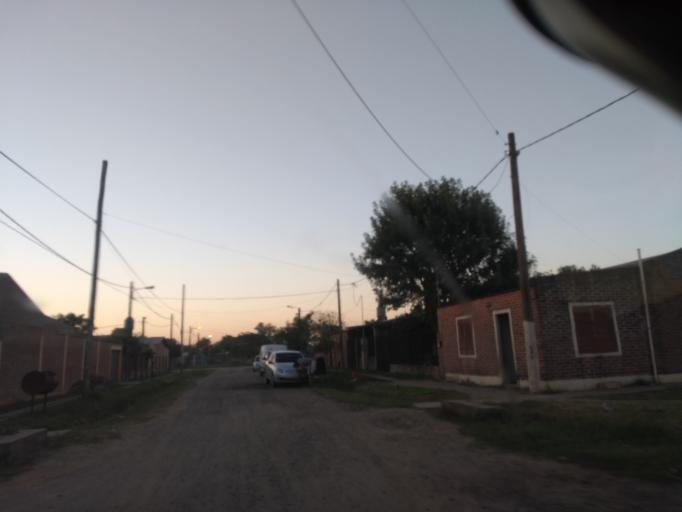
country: AR
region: Chaco
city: Fontana
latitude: -27.4160
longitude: -59.0465
